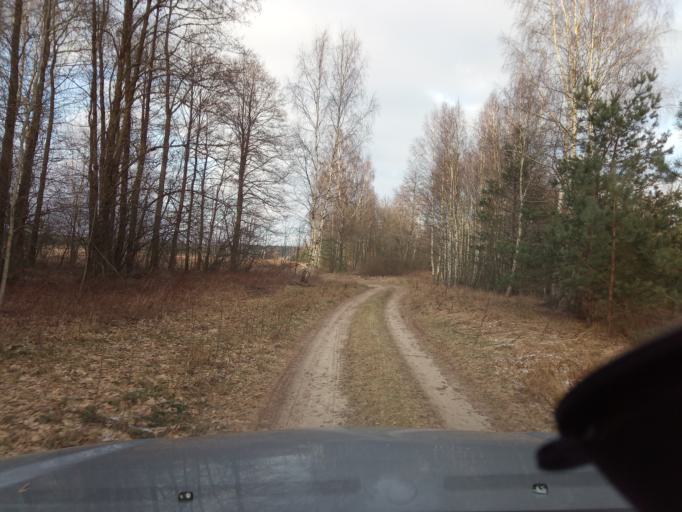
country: LT
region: Alytaus apskritis
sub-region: Alytaus rajonas
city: Daugai
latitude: 54.1115
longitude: 24.2397
